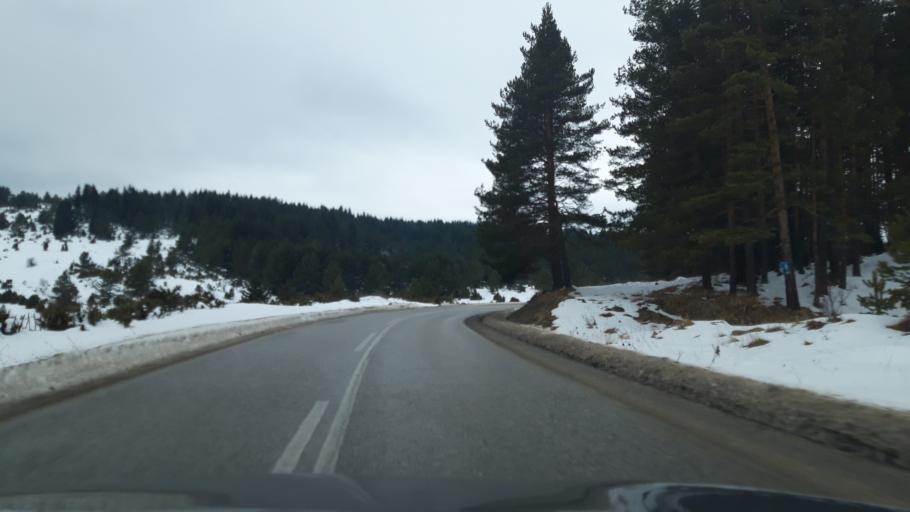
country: BA
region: Republika Srpska
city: Sokolac
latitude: 43.9099
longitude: 18.7043
